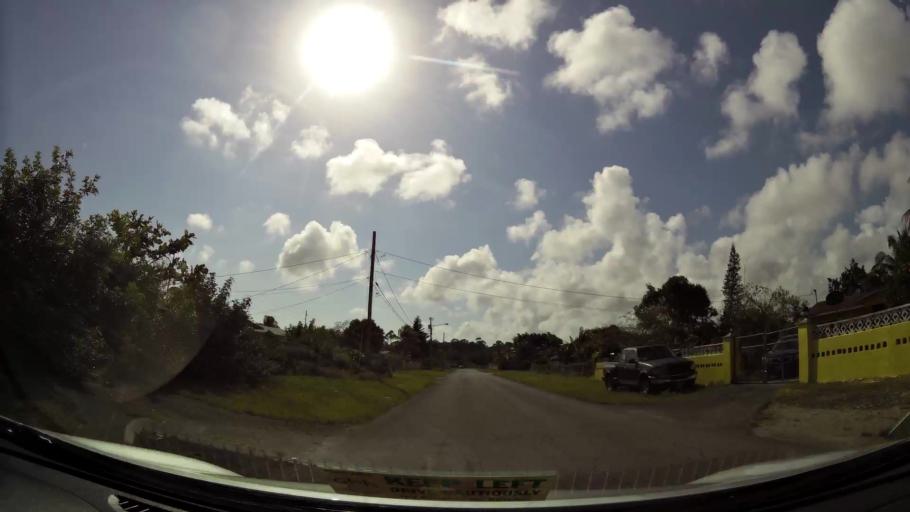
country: BS
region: Freeport
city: Lucaya
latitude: 26.5245
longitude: -78.6818
